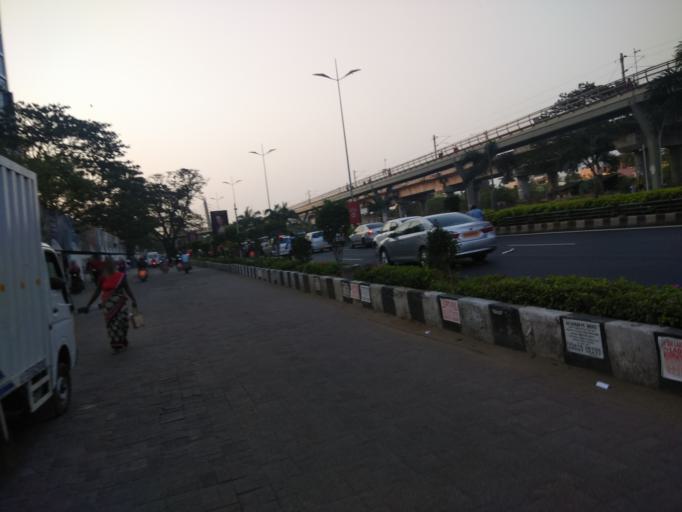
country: IN
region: Tamil Nadu
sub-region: Chennai
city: Gandhi Nagar
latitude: 12.9904
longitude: 80.2506
